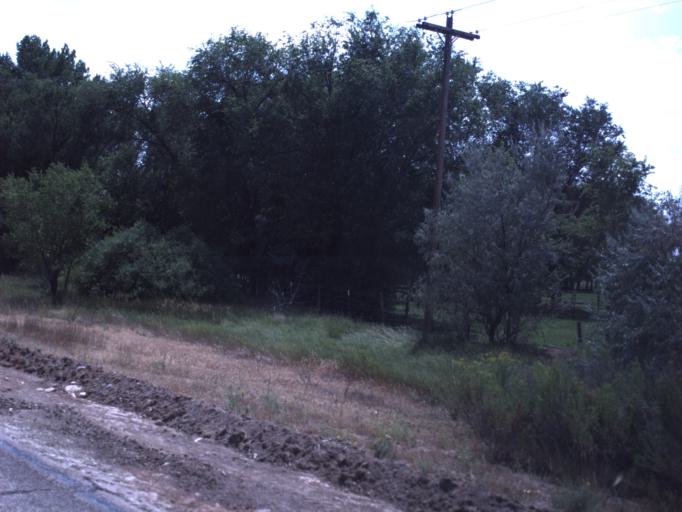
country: US
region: Utah
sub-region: Duchesne County
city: Roosevelt
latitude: 40.3503
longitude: -110.0296
